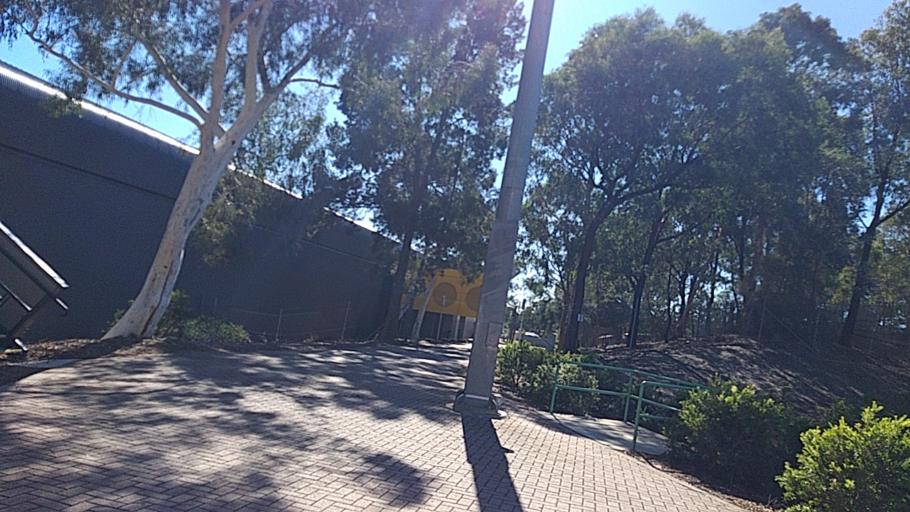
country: AU
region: Australian Capital Territory
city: Kaleen
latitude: -35.2458
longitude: 149.1044
